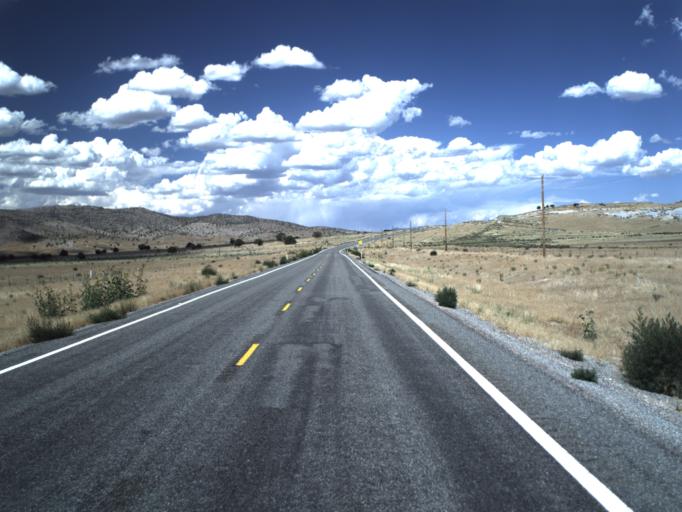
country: US
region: Utah
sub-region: Millard County
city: Delta
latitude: 39.6401
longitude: -112.3046
